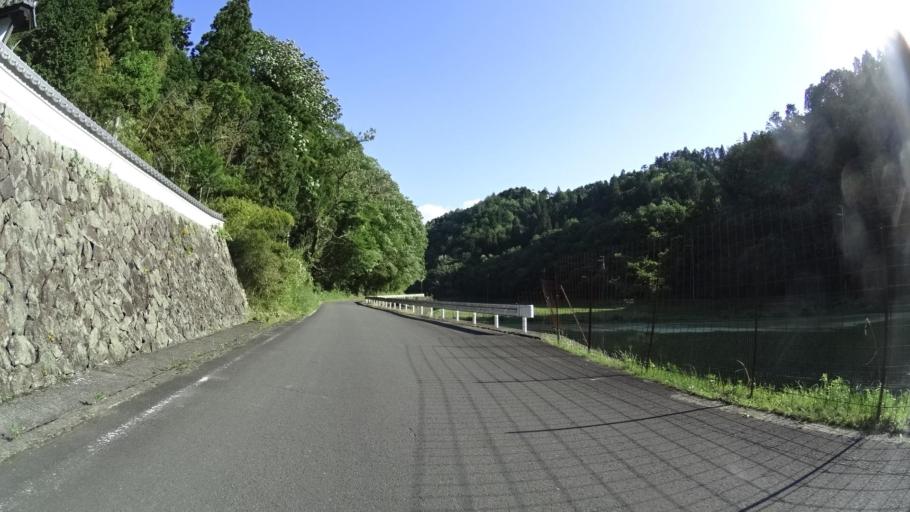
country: JP
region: Kyoto
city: Kameoka
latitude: 34.9764
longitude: 135.5607
